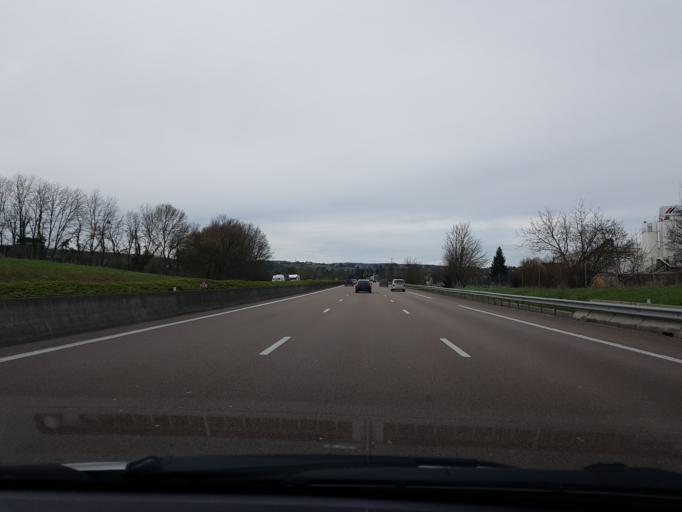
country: FR
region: Bourgogne
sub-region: Departement de Saone-et-Loire
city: Tournus
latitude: 46.5509
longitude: 4.9090
